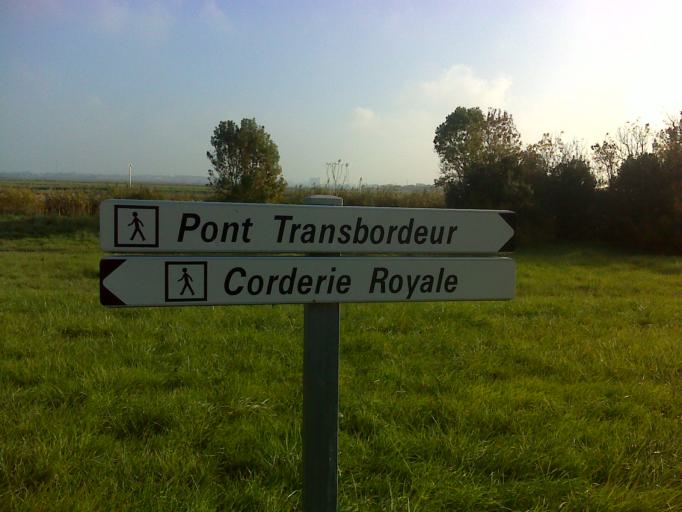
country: FR
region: Poitou-Charentes
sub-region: Departement de la Charente-Maritime
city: Echillais
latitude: 45.9269
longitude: -0.9495
